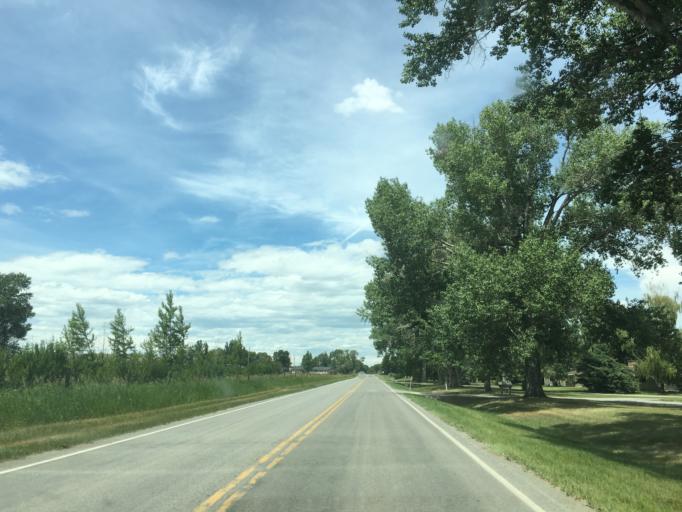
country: US
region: Montana
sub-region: Teton County
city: Choteau
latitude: 47.8245
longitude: -112.1930
